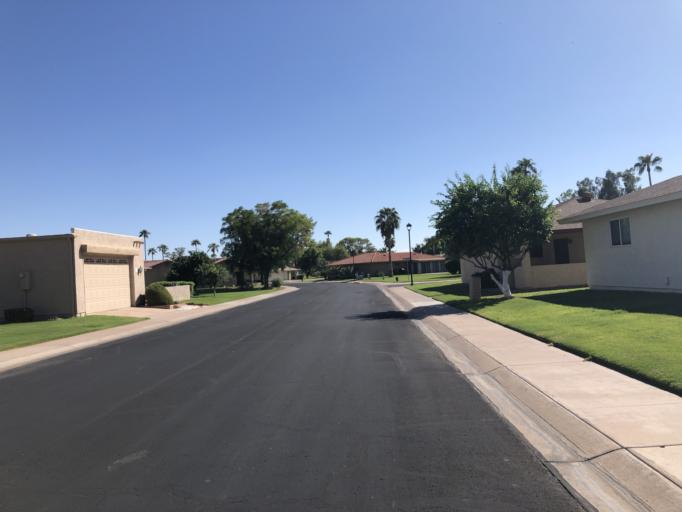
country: US
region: Arizona
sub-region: Maricopa County
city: Gilbert
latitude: 33.4026
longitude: -111.6912
